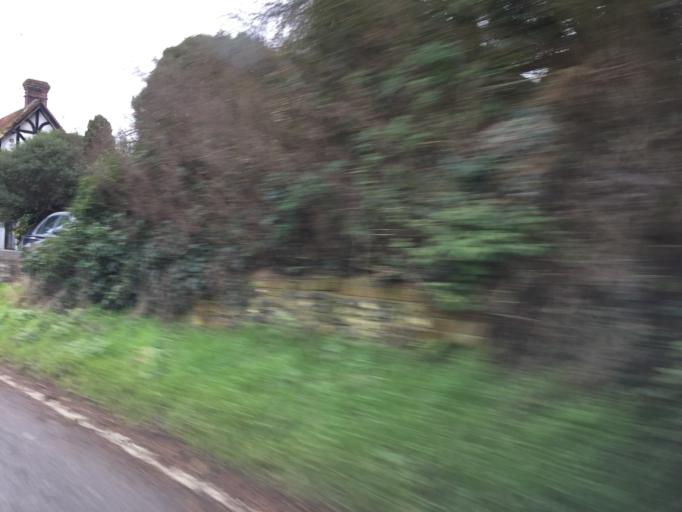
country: GB
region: England
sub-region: West Berkshire
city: Basildon
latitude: 51.5070
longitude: -1.1275
